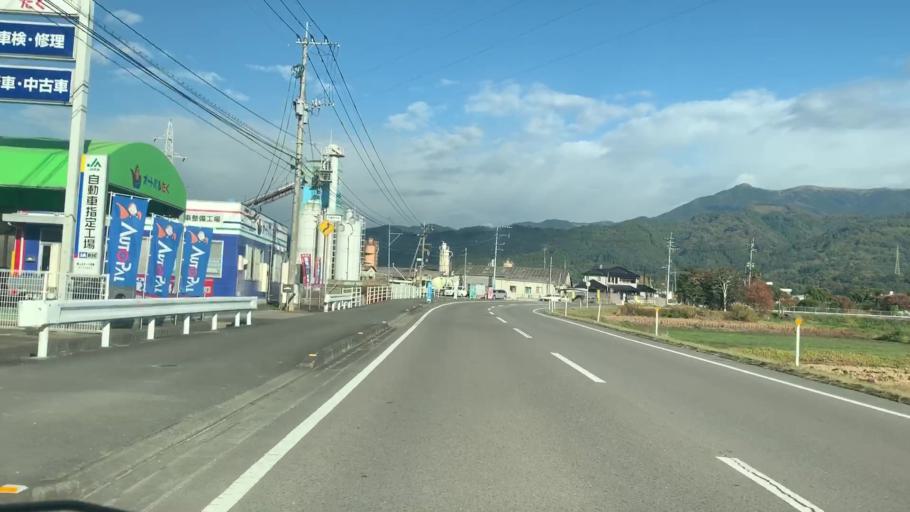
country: JP
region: Saga Prefecture
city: Takeocho-takeo
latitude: 33.2777
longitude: 130.1449
